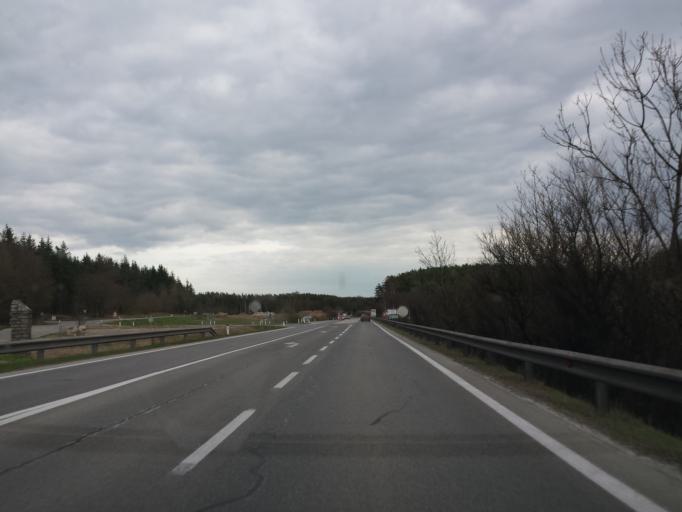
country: AT
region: Lower Austria
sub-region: Politischer Bezirk Krems
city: Lengenfeld
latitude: 48.4929
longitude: 15.5733
